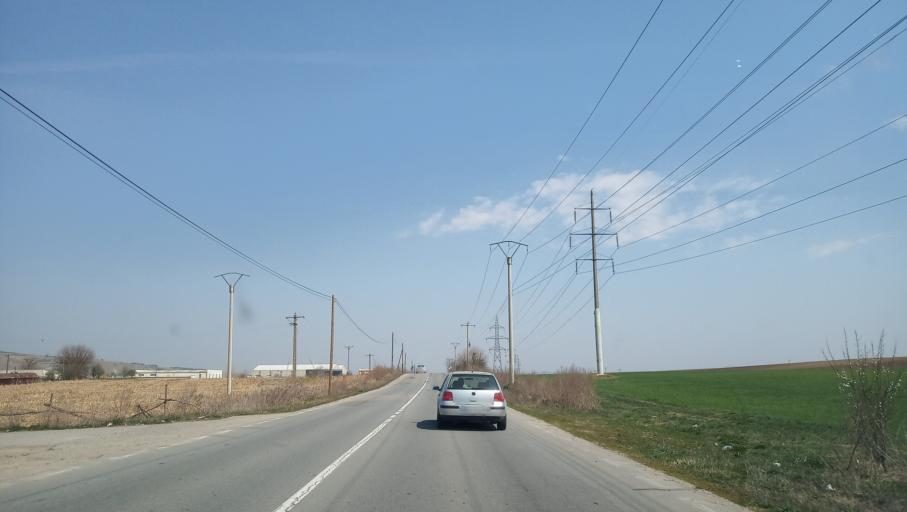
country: RO
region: Alba
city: Vurpar
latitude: 46.0097
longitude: 23.5049
